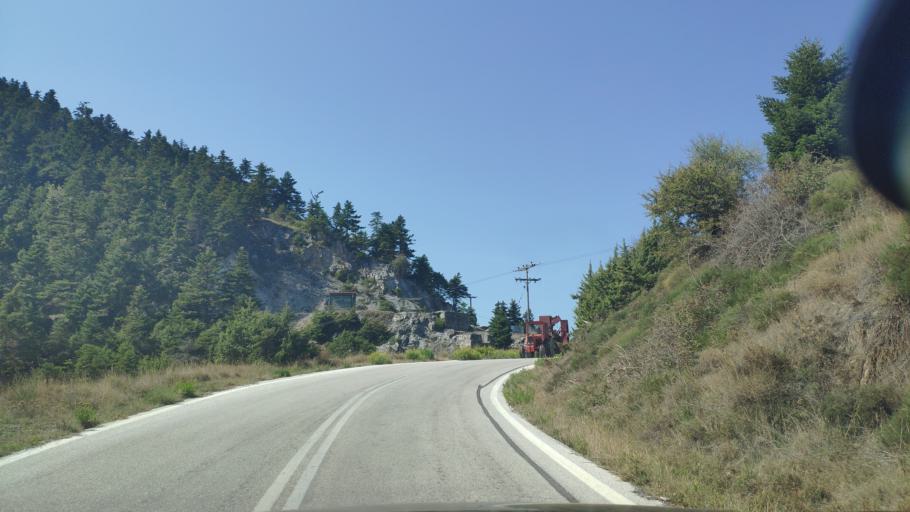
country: GR
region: West Greece
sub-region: Nomos Achaias
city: Aiyira
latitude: 37.8654
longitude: 22.3680
